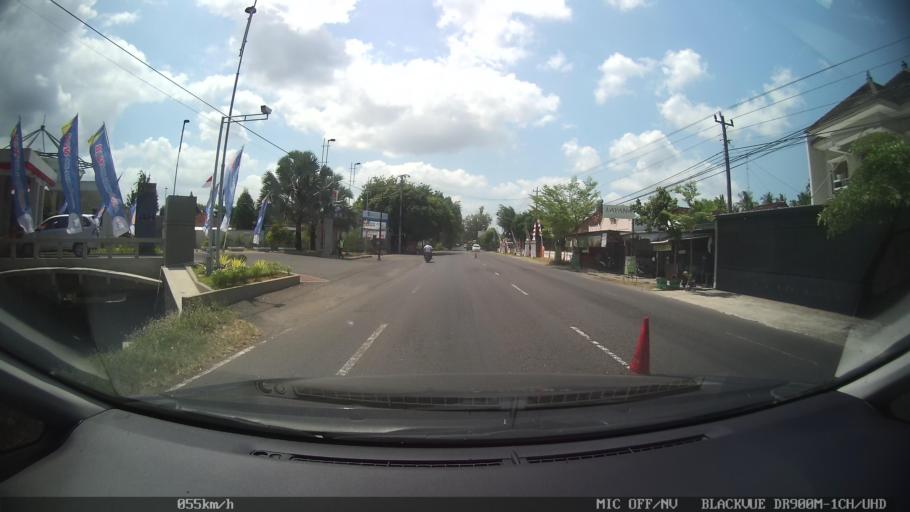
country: ID
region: Daerah Istimewa Yogyakarta
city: Pandak
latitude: -7.9099
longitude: 110.2963
